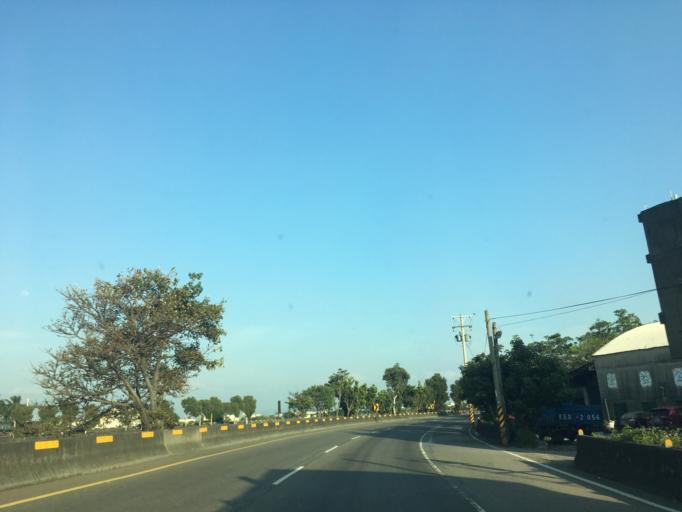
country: TW
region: Taiwan
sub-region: Changhua
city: Chang-hua
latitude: 24.0453
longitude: 120.4374
